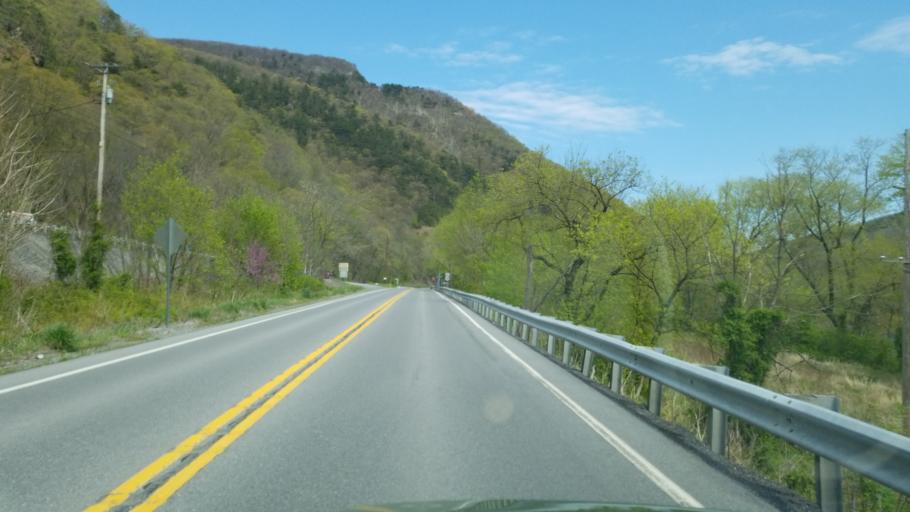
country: US
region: Pennsylvania
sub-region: Huntingdon County
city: Mount Union
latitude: 40.3948
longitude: -77.9270
